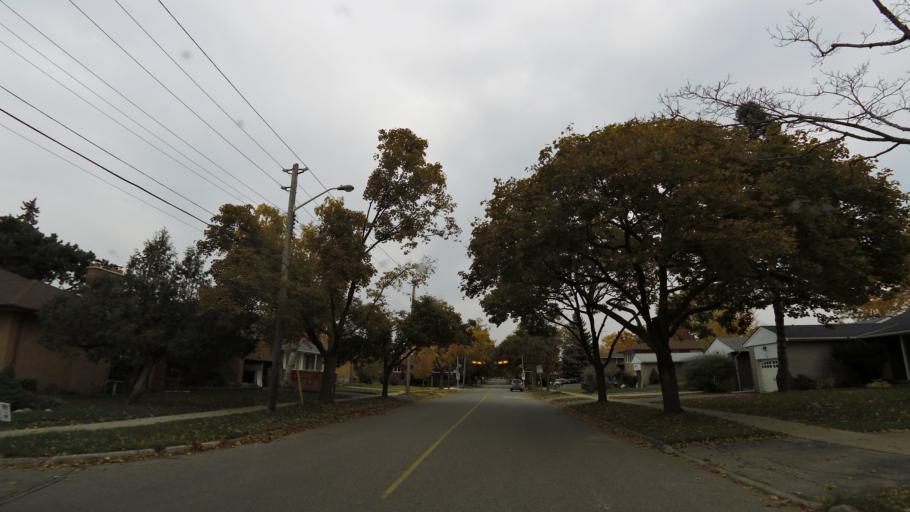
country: CA
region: Ontario
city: Etobicoke
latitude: 43.6840
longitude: -79.5364
